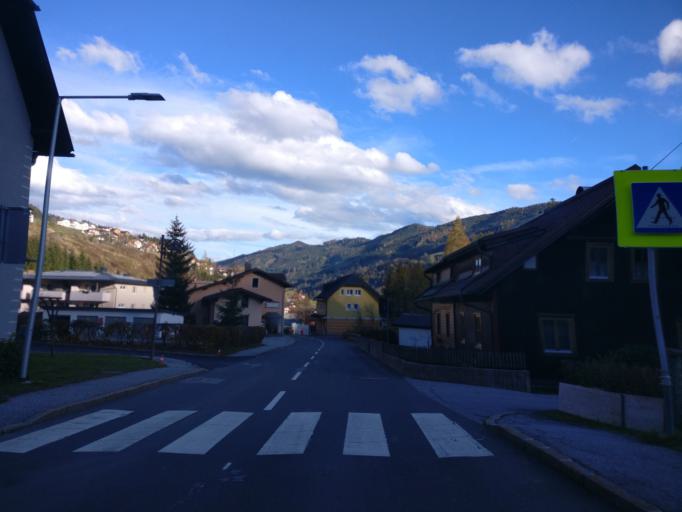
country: AT
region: Salzburg
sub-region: Politischer Bezirk Sankt Johann im Pongau
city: Muhlbach am Hochkonig
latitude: 47.3779
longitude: 13.1180
